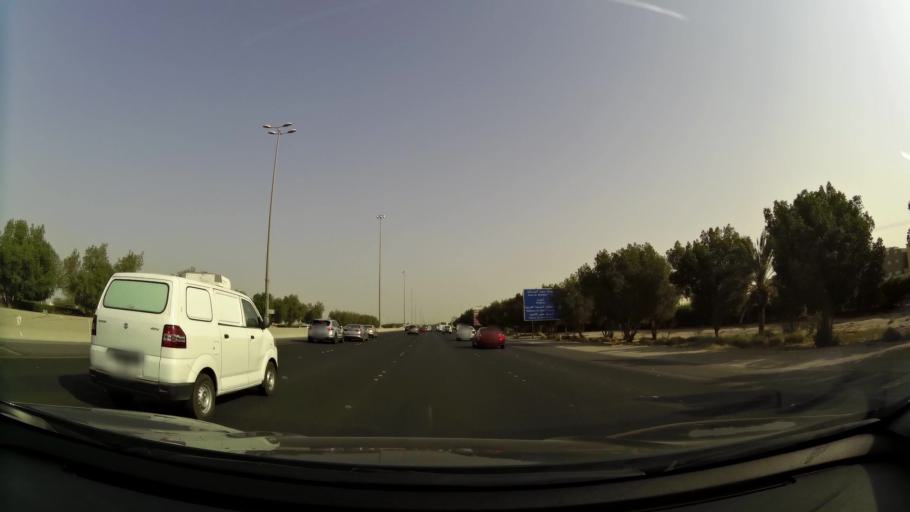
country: KW
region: Muhafazat al Jahra'
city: Al Jahra'
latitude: 29.3274
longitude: 47.7422
